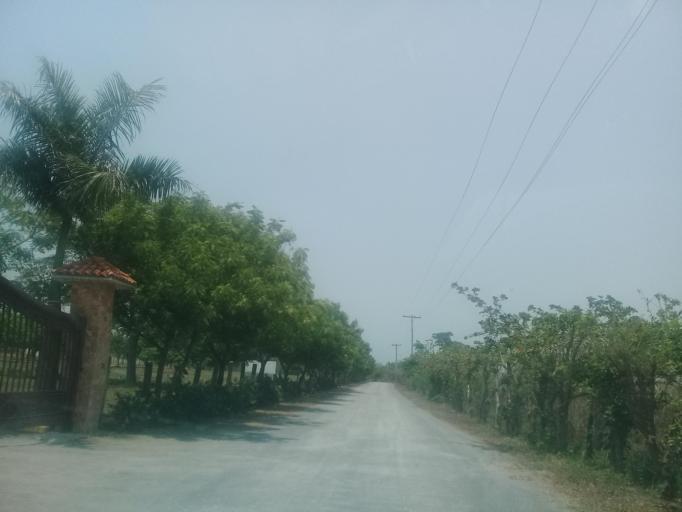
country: MX
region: Veracruz
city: Jamapa
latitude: 19.0849
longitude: -96.2365
